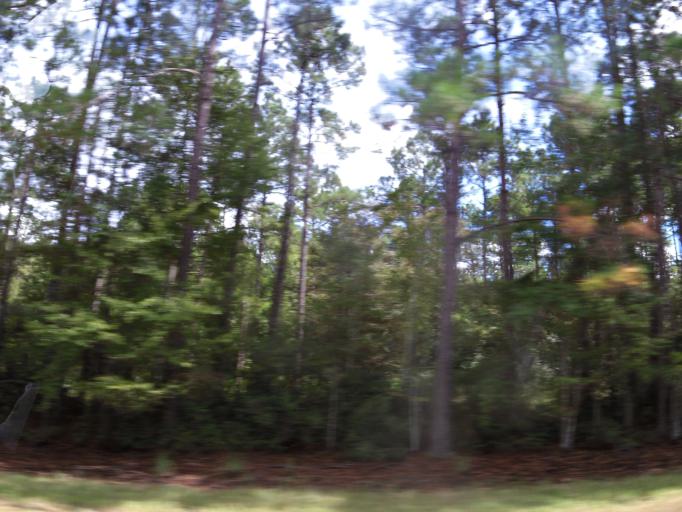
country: US
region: Georgia
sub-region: Brantley County
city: Nahunta
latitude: 31.1254
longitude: -82.0002
